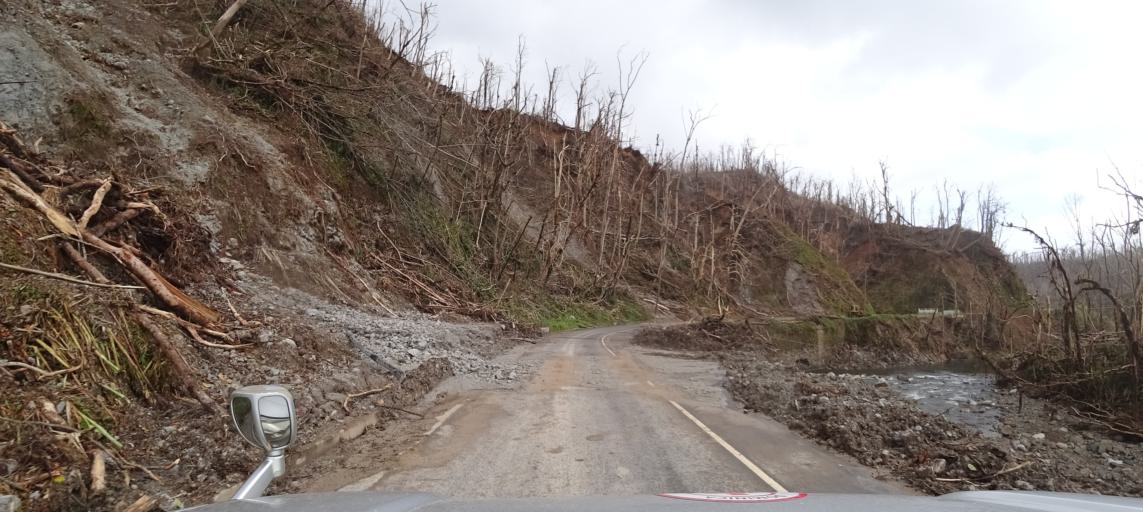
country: DM
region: Saint Paul
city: Pont Casse
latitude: 15.4298
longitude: -61.3334
